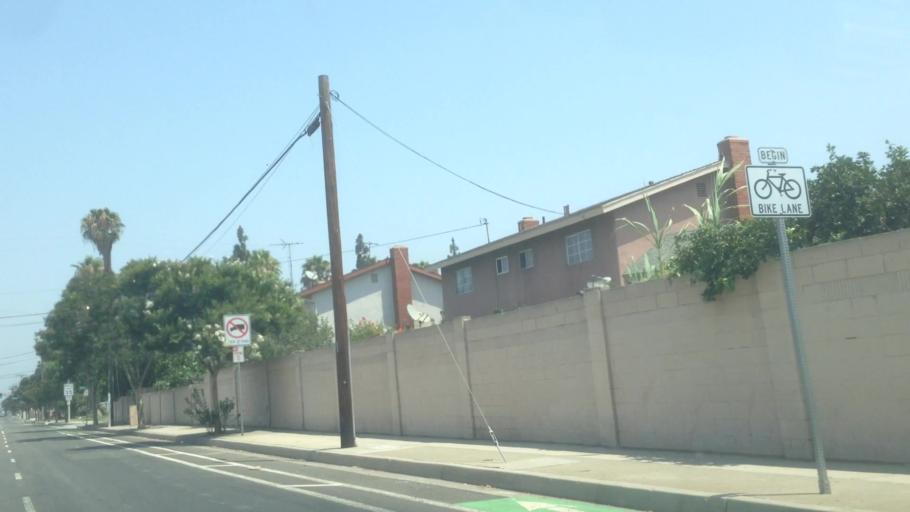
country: US
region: California
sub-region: Orange County
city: Garden Grove
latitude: 33.7384
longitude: -117.9287
